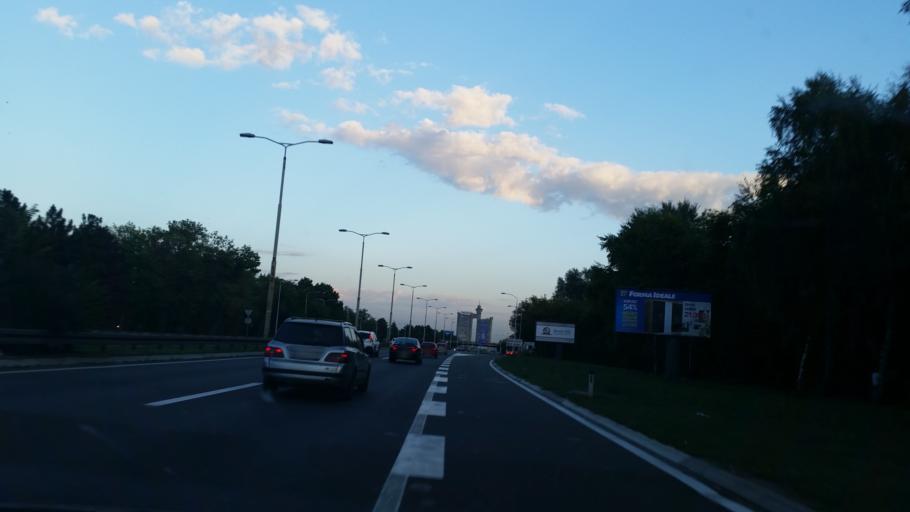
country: RS
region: Central Serbia
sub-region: Belgrade
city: Zemun
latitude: 44.8277
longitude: 20.3861
